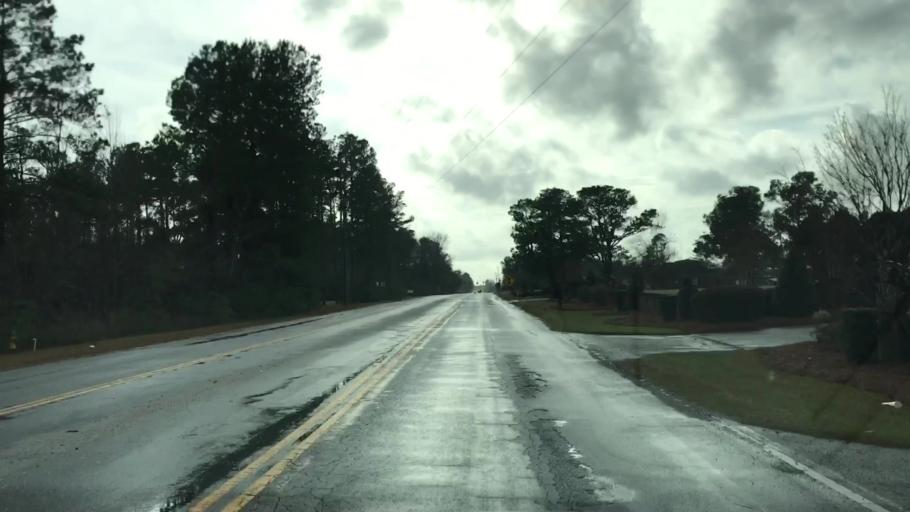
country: US
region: South Carolina
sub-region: Williamsburg County
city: Andrews
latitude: 33.4608
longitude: -79.5727
